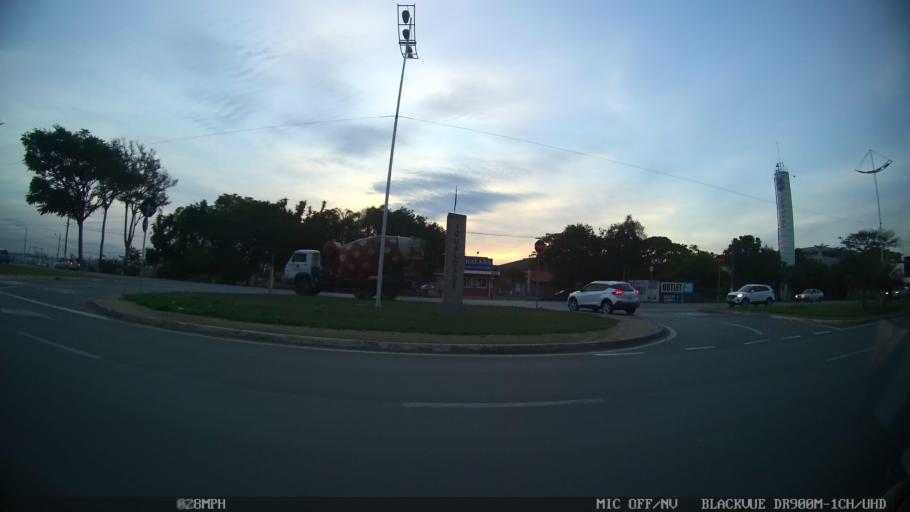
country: BR
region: Sao Paulo
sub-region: Limeira
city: Limeira
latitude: -22.5488
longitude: -47.3786
